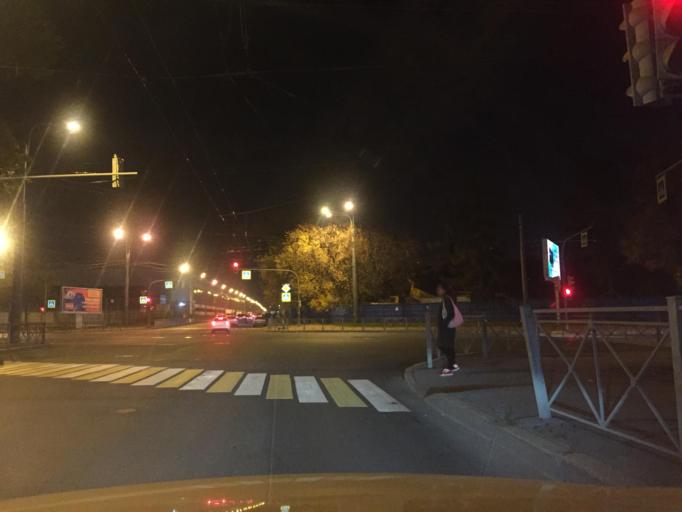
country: RU
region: St.-Petersburg
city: Kushelevka
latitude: 59.9940
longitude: 30.3583
